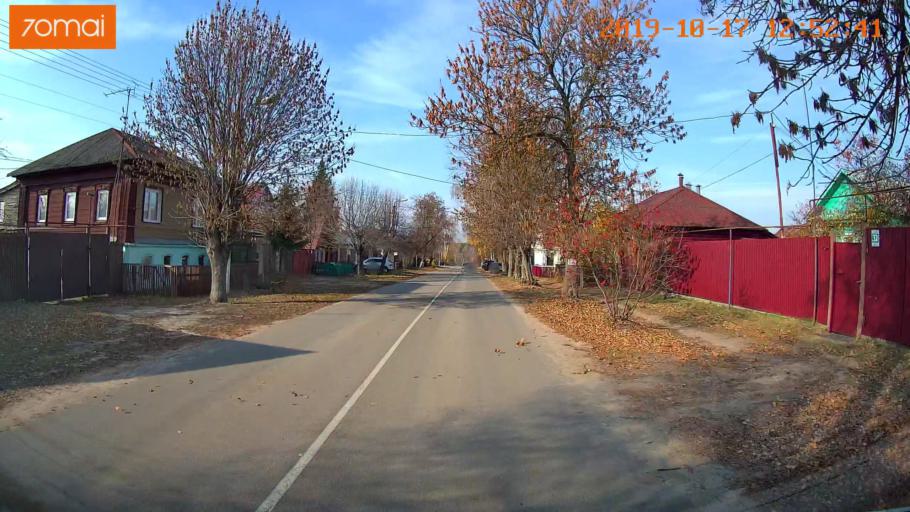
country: RU
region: Rjazan
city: Kasimov
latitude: 54.9434
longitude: 41.3879
